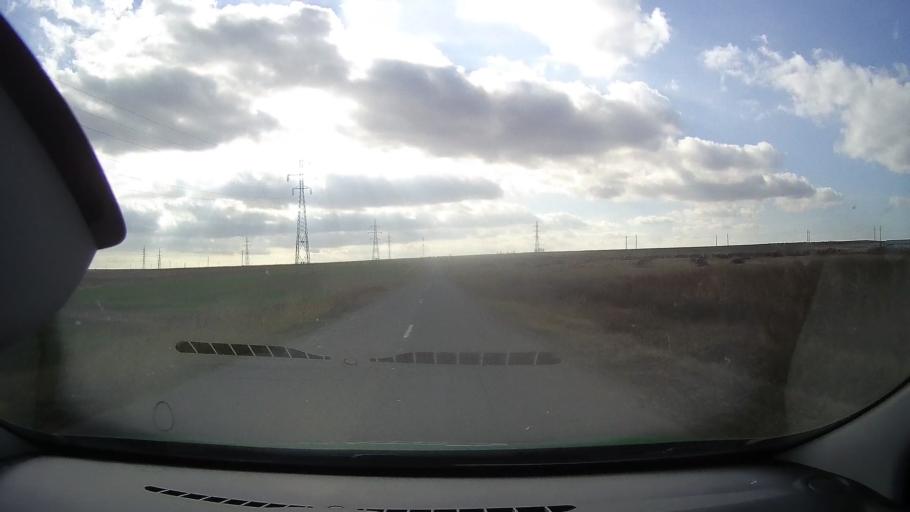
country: RO
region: Constanta
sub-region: Comuna Sacele
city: Sacele
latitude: 44.4976
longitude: 28.6588
